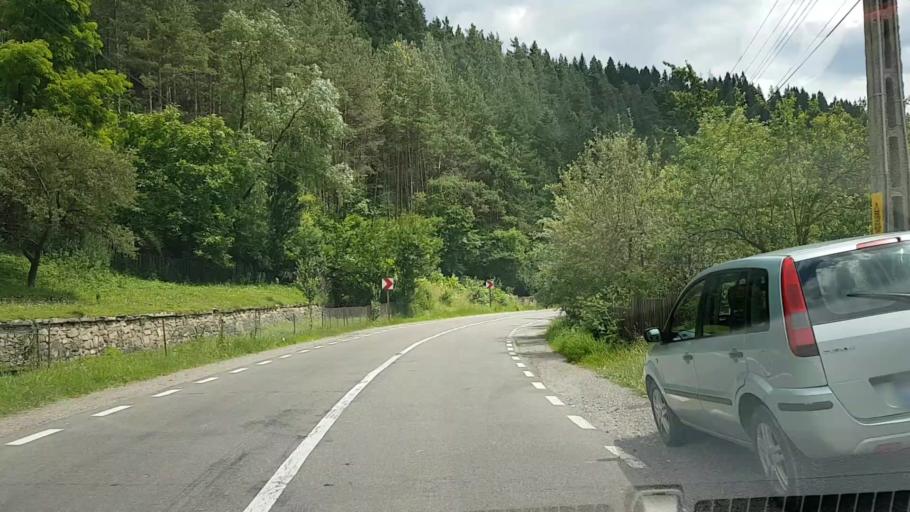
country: RO
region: Neamt
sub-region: Comuna Poiana Teiului
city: Poiana Teiului
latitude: 47.1276
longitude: 25.9051
